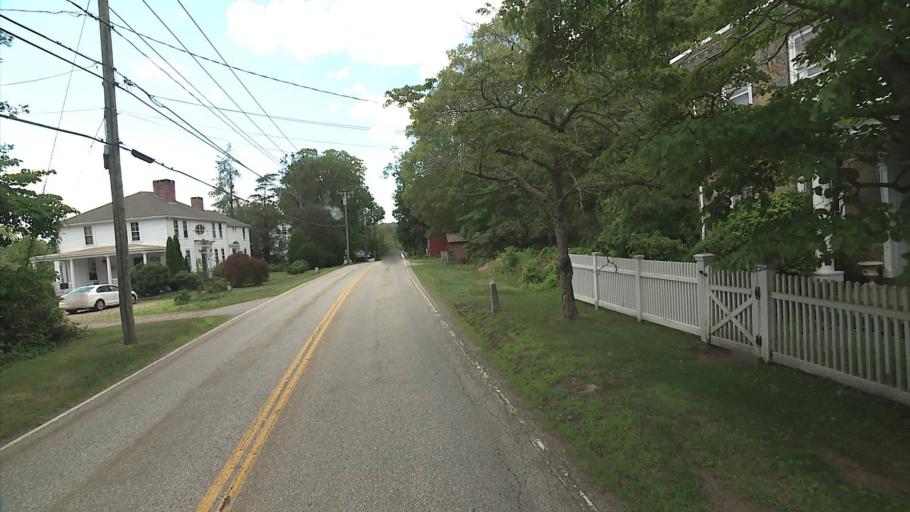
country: US
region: Connecticut
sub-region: Middlesex County
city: East Hampton
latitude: 41.5500
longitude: -72.5485
